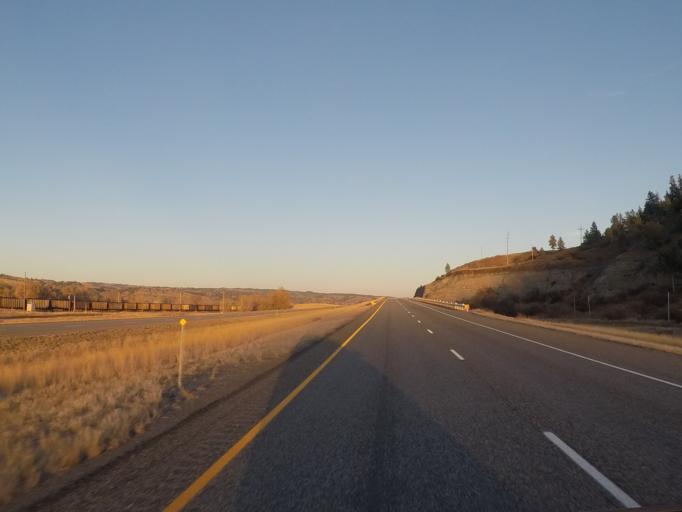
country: US
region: Montana
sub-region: Sweet Grass County
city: Big Timber
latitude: 45.7335
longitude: -109.7311
